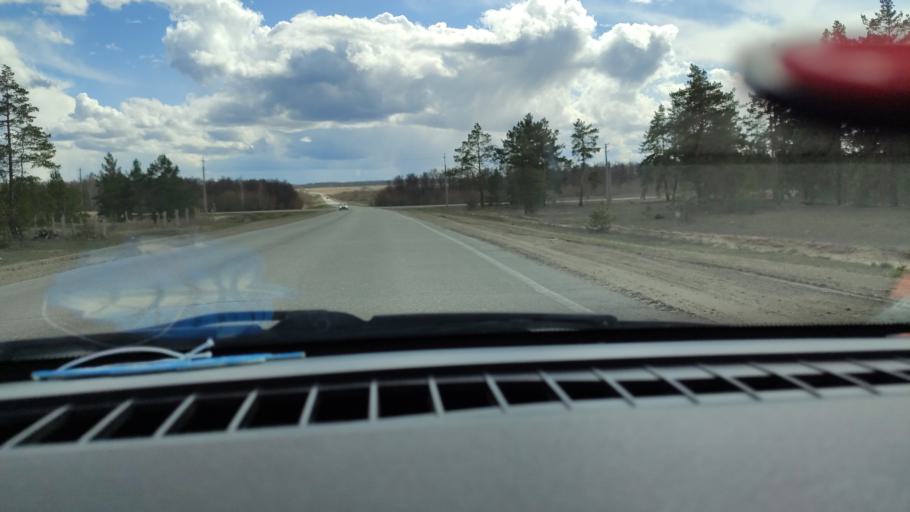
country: RU
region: Samara
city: Varlamovo
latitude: 53.1440
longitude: 48.2851
